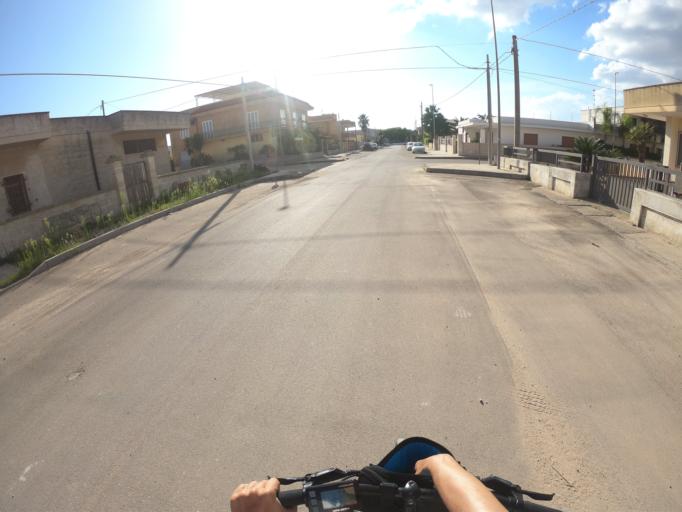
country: IT
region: Apulia
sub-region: Provincia di Lecce
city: Nardo
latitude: 40.1606
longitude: 18.0220
